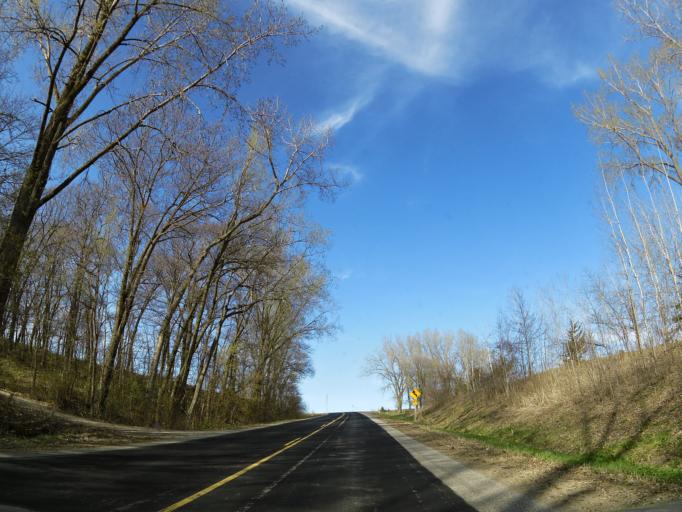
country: US
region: Minnesota
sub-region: Goodhue County
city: Red Wing
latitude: 44.6692
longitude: -92.6066
